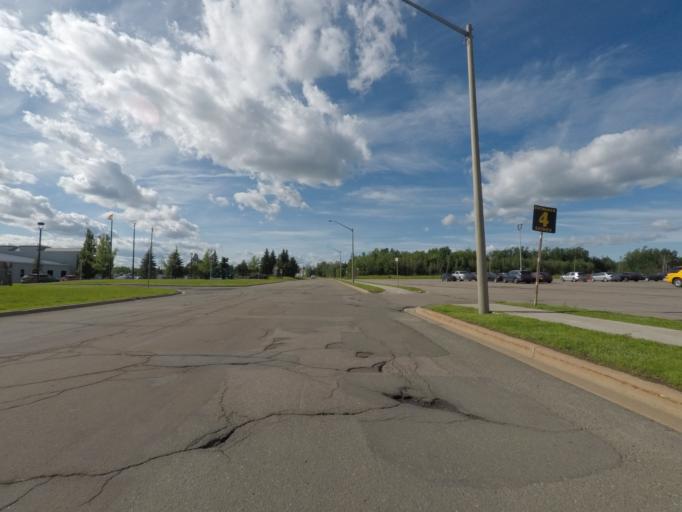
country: CA
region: New Brunswick
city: Moncton
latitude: 46.0957
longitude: -64.8328
